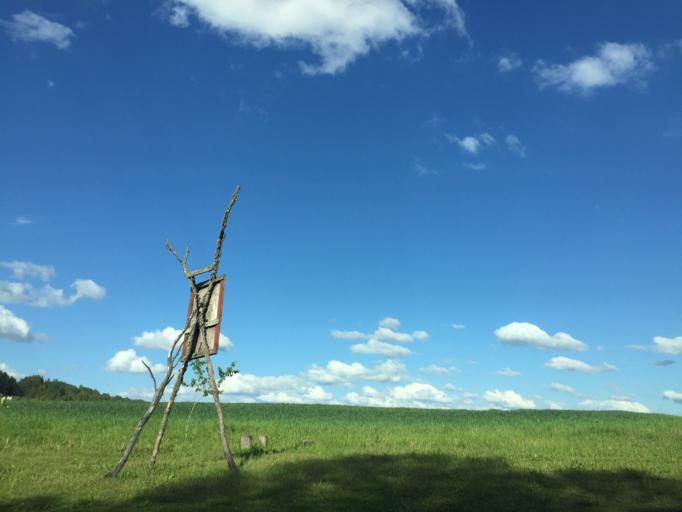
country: LV
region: Talsu Rajons
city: Sabile
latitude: 57.0141
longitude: 22.6241
